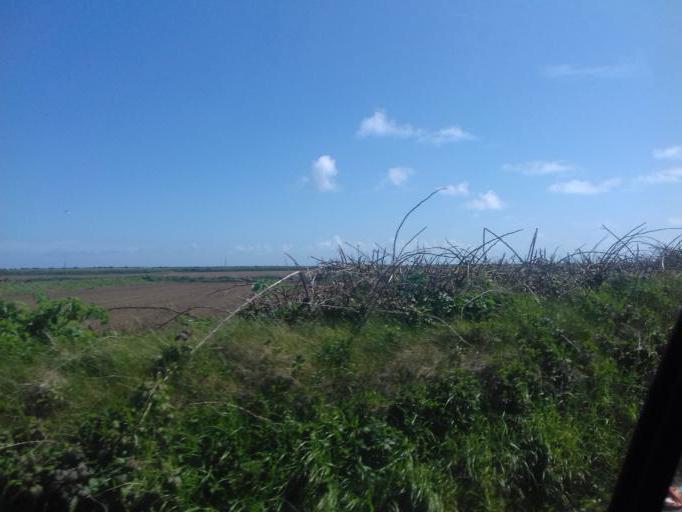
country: IE
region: Munster
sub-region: Waterford
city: Dunmore East
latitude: 52.1318
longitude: -6.9295
